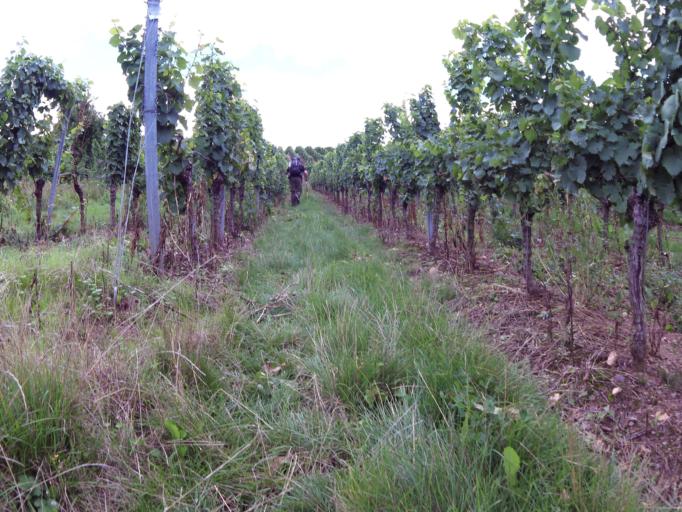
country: DE
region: Rheinland-Pfalz
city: Niederhausen
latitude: 49.8081
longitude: 7.7816
